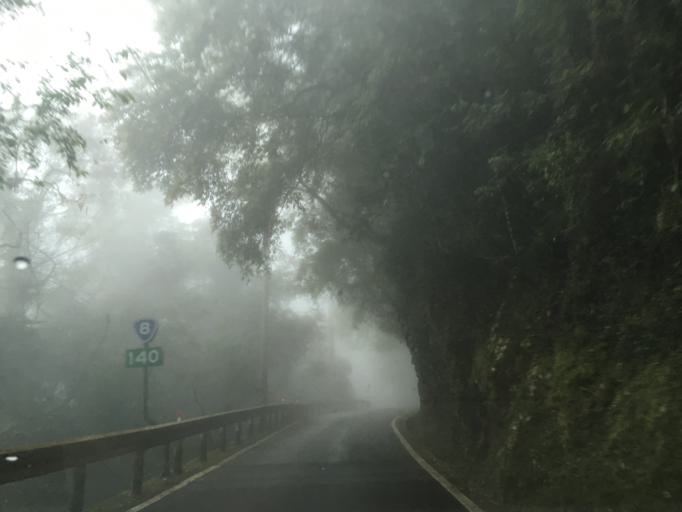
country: TW
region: Taiwan
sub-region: Hualien
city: Hualian
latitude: 24.1933
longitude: 121.4175
